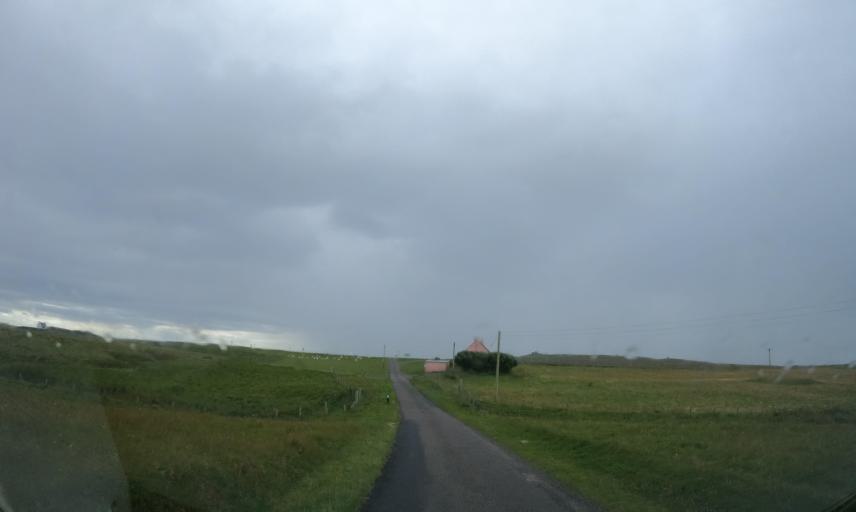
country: GB
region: Scotland
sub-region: Eilean Siar
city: Barra
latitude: 56.5145
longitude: -6.8163
